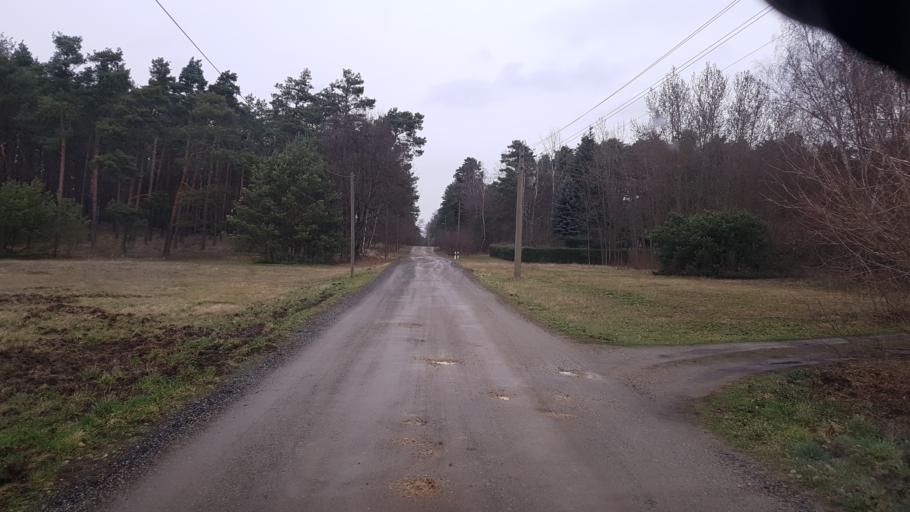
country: DE
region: Brandenburg
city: Crinitz
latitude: 51.7425
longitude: 13.7666
